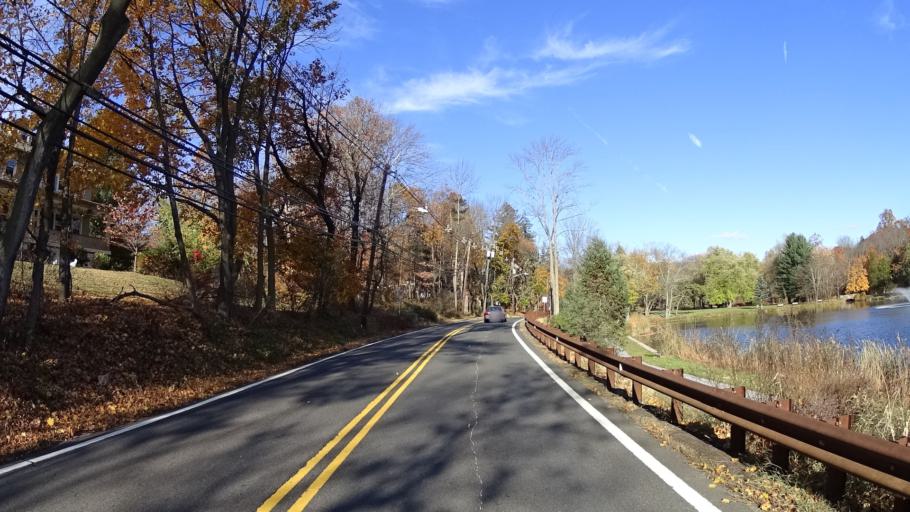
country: US
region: New Jersey
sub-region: Somerset County
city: Watchung
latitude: 40.6395
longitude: -74.4498
